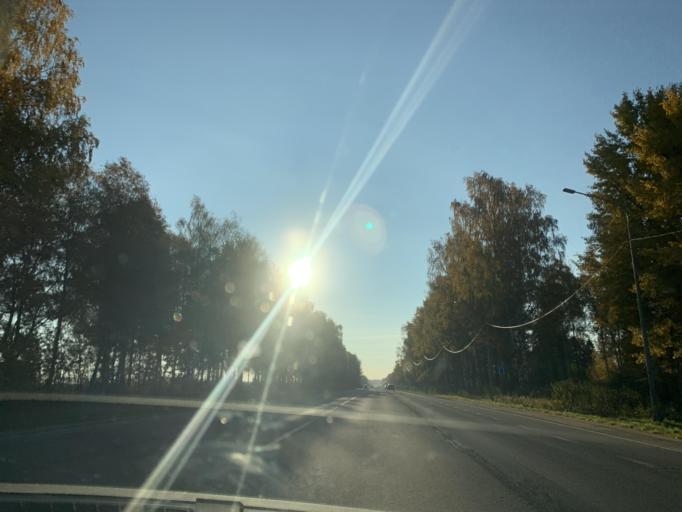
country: RU
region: Jaroslavl
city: Konstantinovskiy
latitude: 57.7511
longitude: 39.7019
